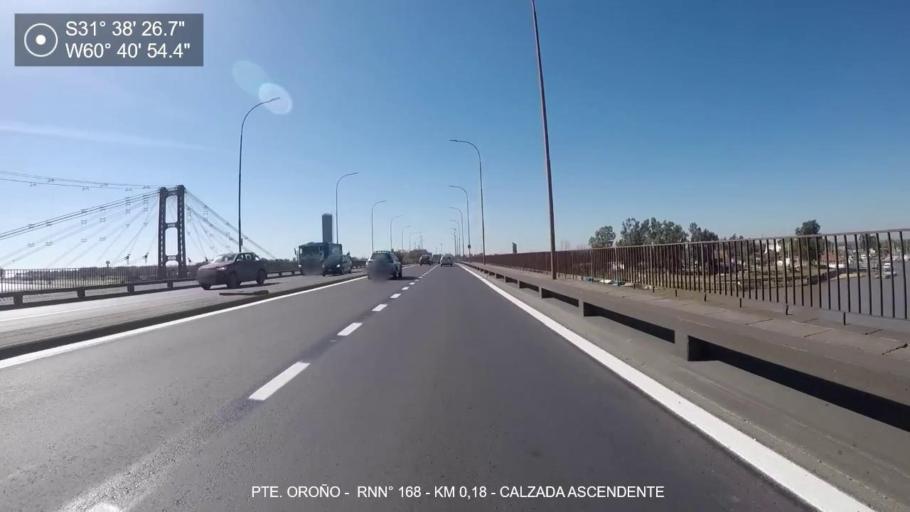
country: AR
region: Santa Fe
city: Santa Fe de la Vera Cruz
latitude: -31.6407
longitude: -60.6819
